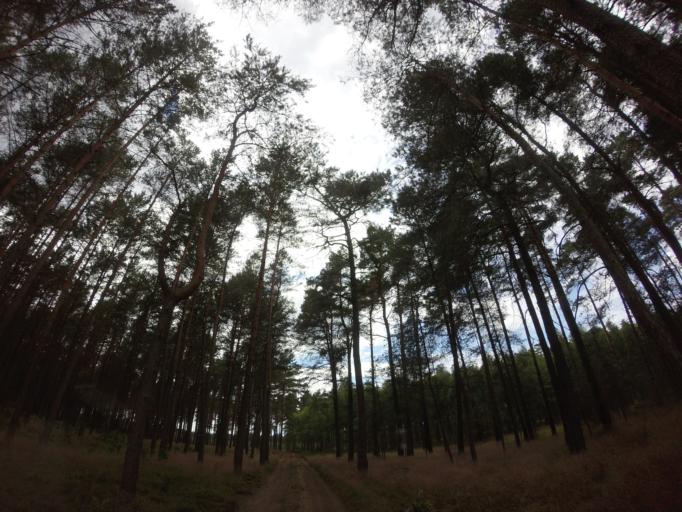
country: PL
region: West Pomeranian Voivodeship
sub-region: Powiat choszczenski
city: Drawno
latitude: 53.1601
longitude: 15.7400
